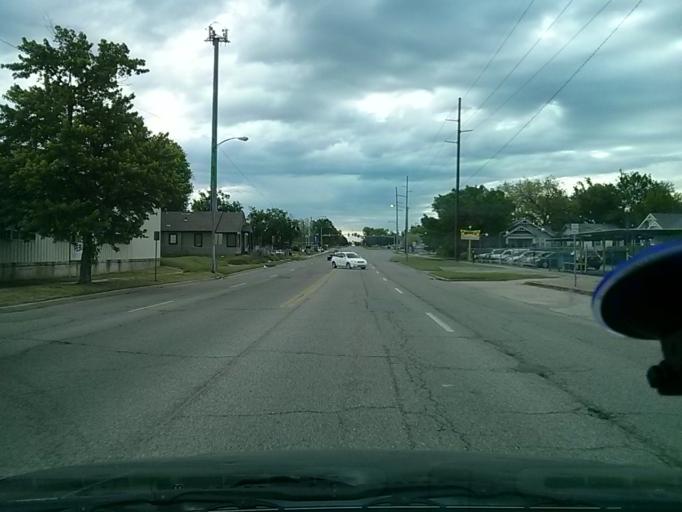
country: US
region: Oklahoma
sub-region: Tulsa County
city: Tulsa
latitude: 36.1566
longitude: -95.9609
